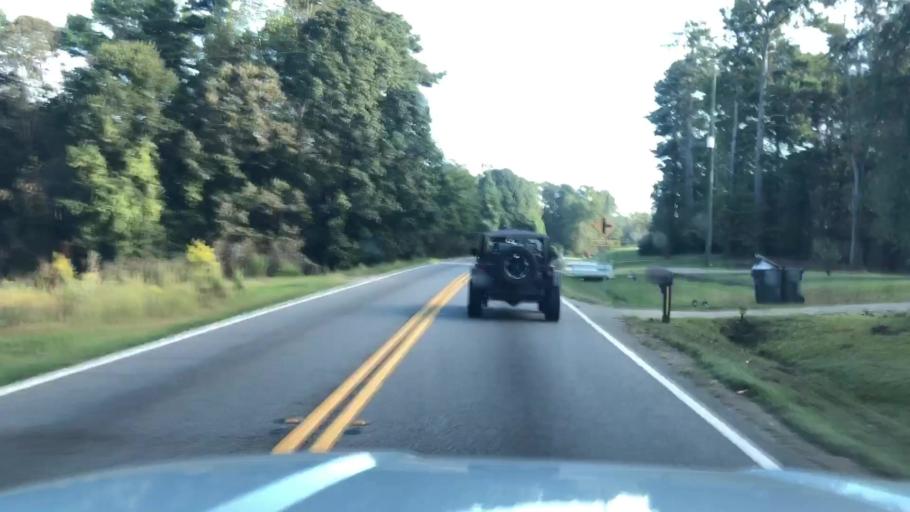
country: US
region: Georgia
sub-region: Cobb County
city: Acworth
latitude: 34.0529
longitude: -84.6962
